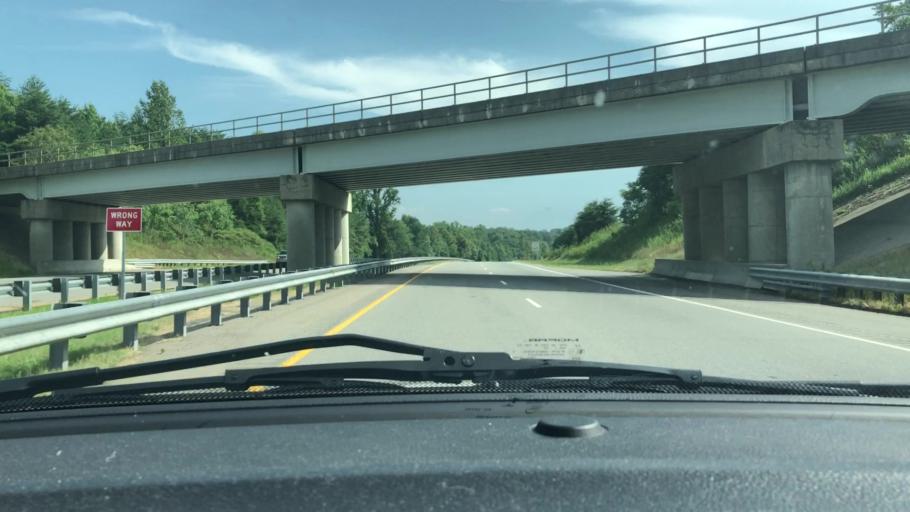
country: US
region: North Carolina
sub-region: Rockingham County
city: Stoneville
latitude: 36.5330
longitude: -79.9140
